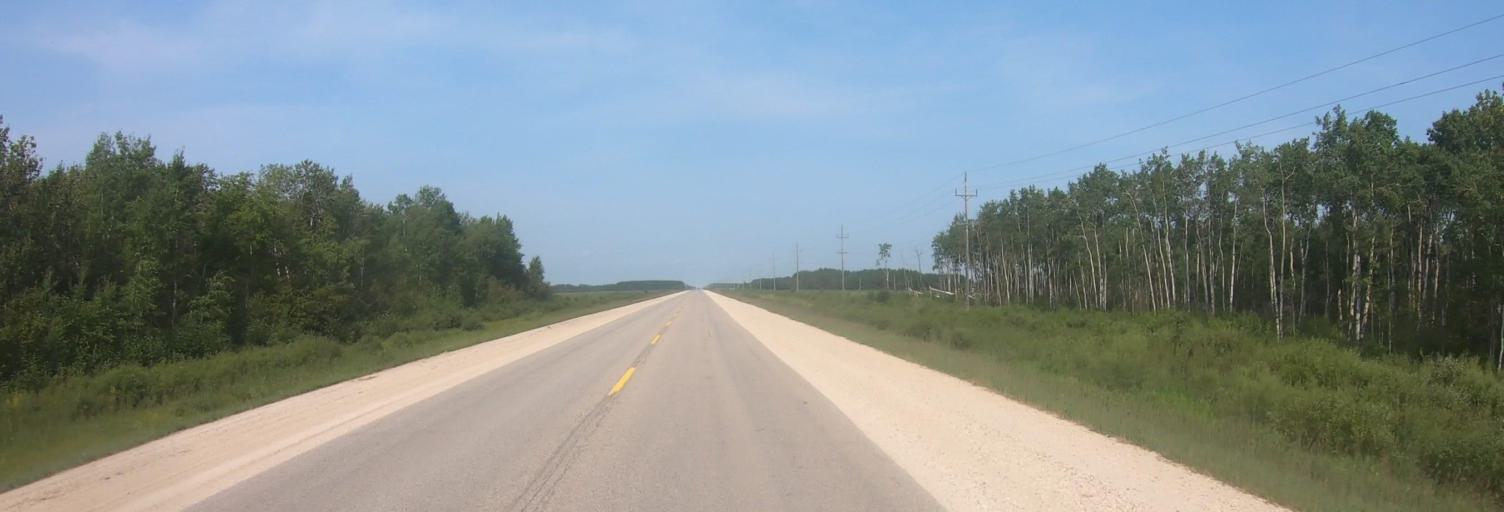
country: CA
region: Manitoba
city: La Broquerie
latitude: 49.2958
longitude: -96.5353
